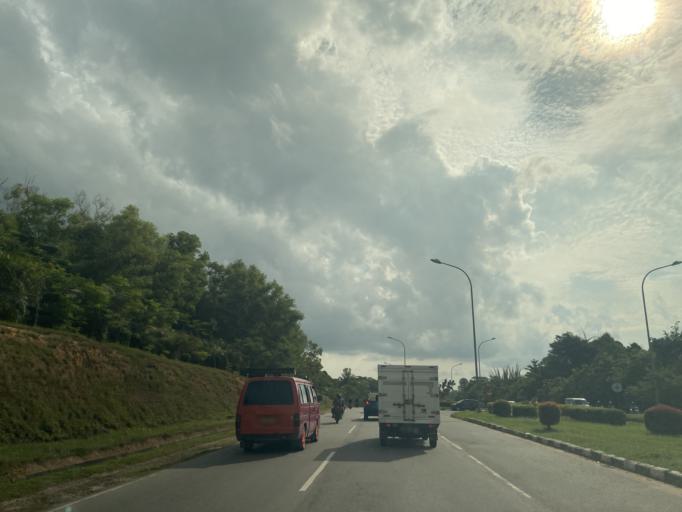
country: SG
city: Singapore
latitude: 1.0990
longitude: 104.0675
